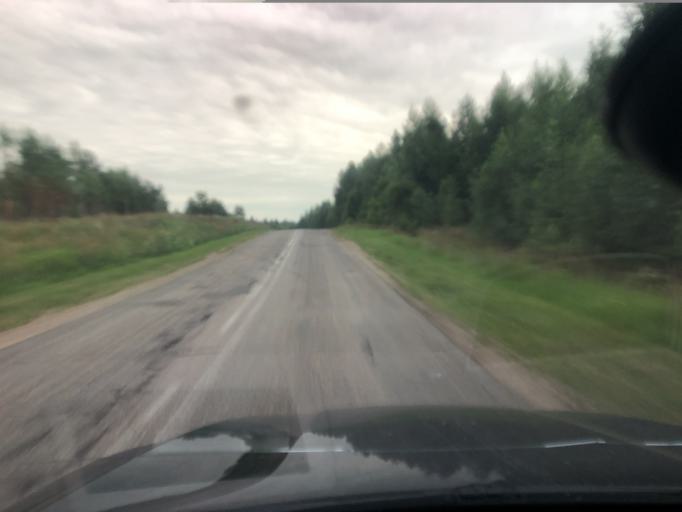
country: RU
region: Jaroslavl
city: Petrovsk
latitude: 57.0009
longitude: 39.0642
